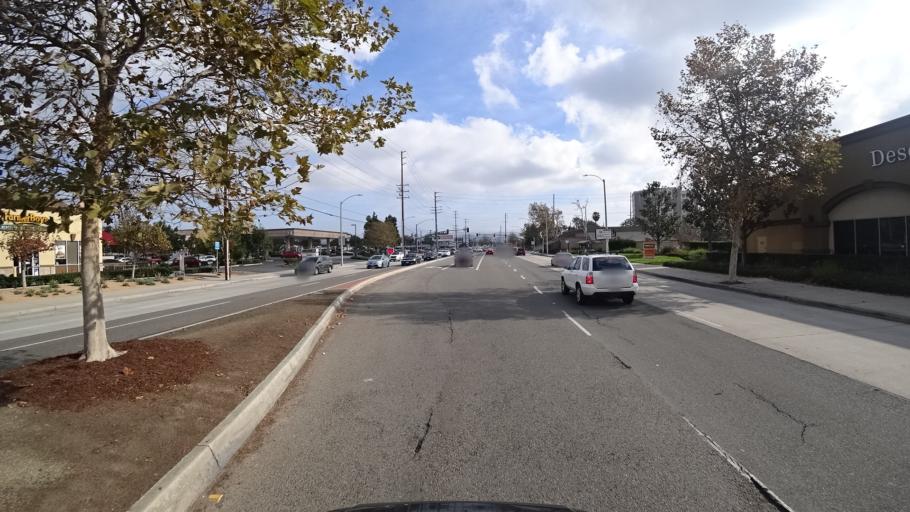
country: US
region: California
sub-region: Orange County
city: Tustin
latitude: 33.7598
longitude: -117.8359
